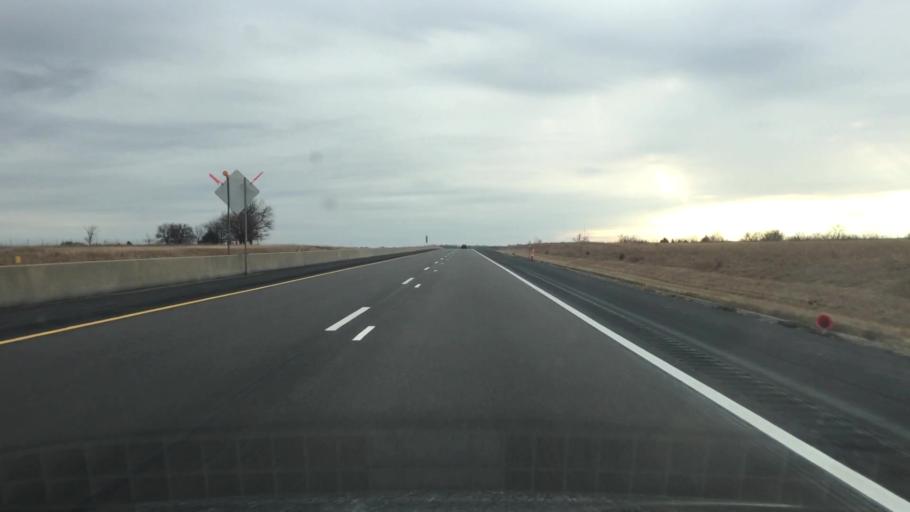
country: US
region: Kansas
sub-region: Osage County
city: Osage City
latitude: 38.6792
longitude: -96.0045
